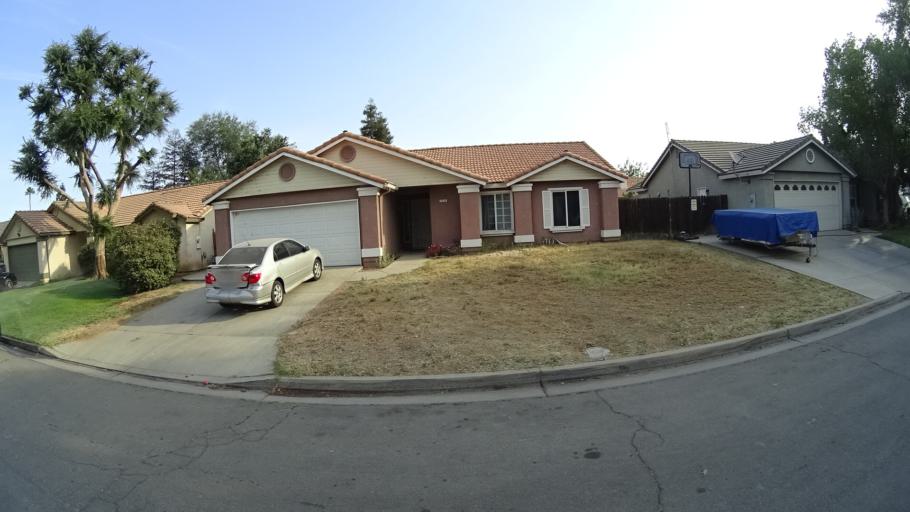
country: US
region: California
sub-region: Fresno County
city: West Park
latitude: 36.7686
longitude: -119.8566
